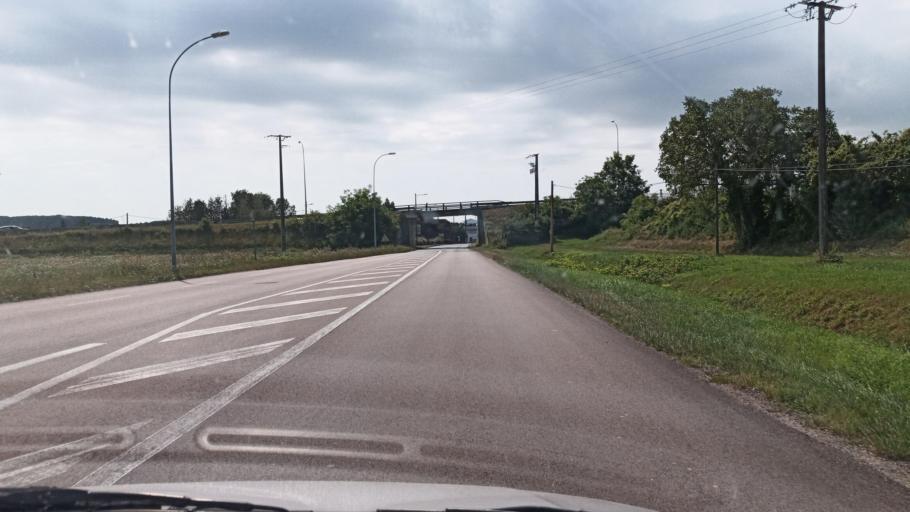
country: FR
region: Bourgogne
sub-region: Departement de l'Yonne
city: Villeneuve-sur-Yonne
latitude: 48.0886
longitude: 3.2867
